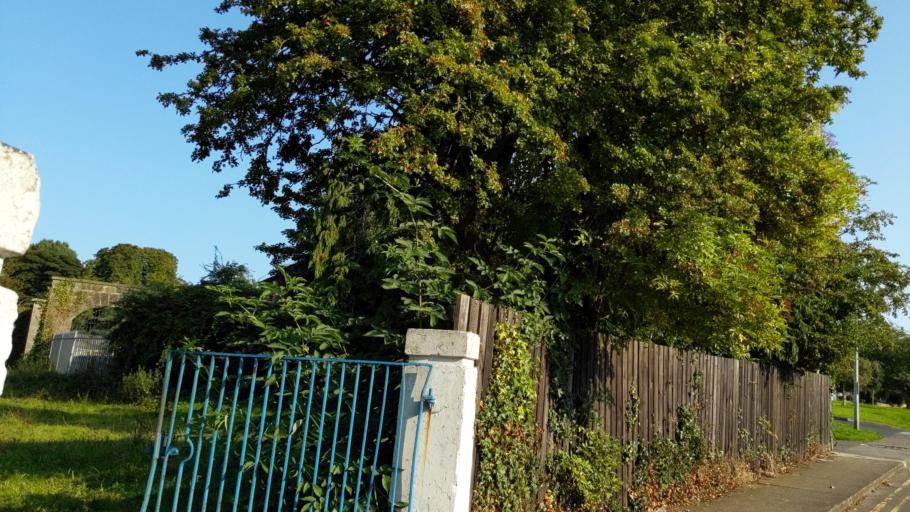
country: IE
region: Leinster
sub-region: Lu
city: Drogheda
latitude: 53.7133
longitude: -6.3607
